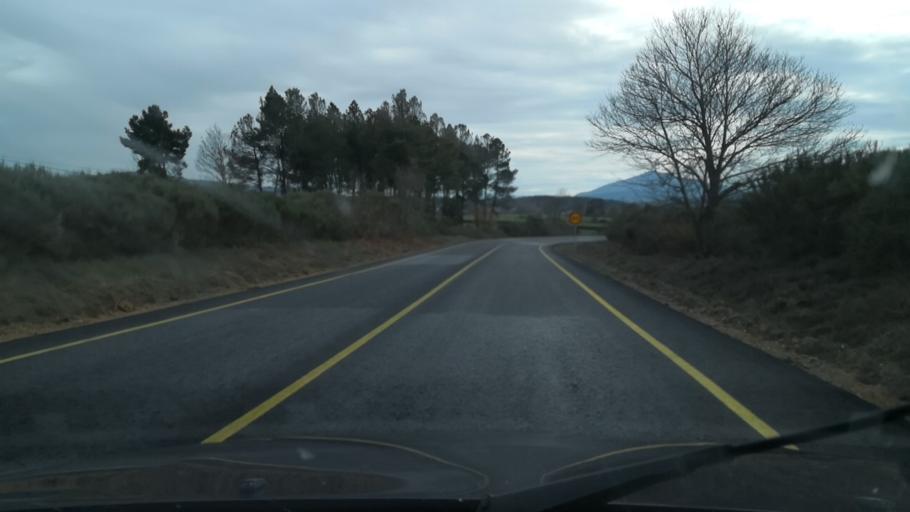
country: ES
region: Castille and Leon
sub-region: Provincia de Salamanca
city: Villasrubias
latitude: 40.3506
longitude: -6.6324
